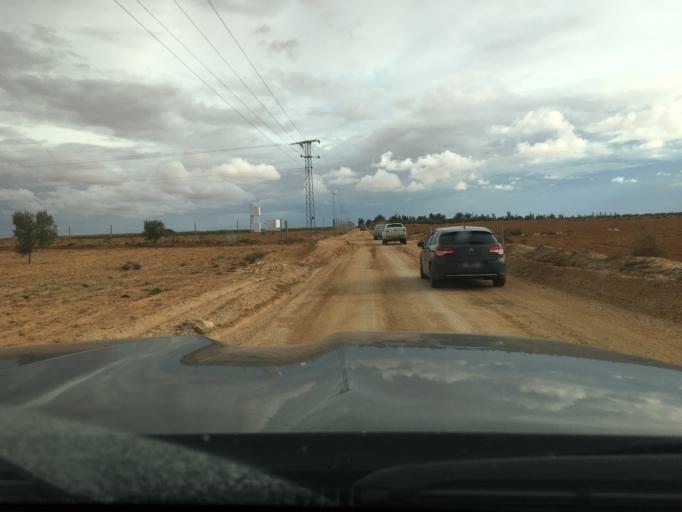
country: TN
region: Madanin
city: Medenine
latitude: 33.2778
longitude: 10.5588
